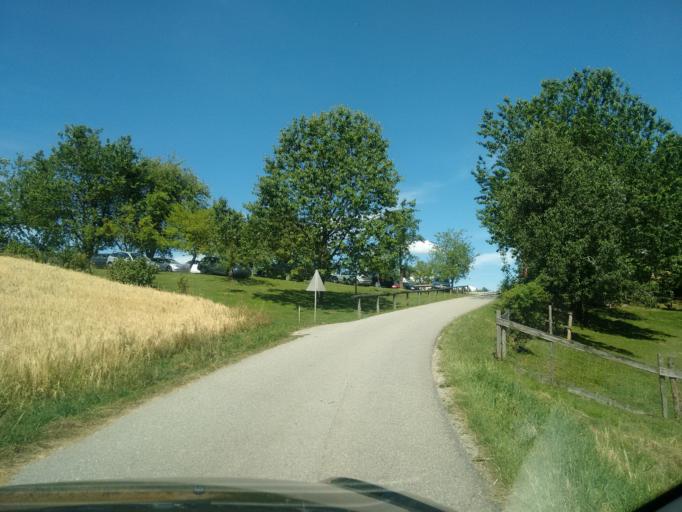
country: AT
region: Upper Austria
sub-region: Politischer Bezirk Ried im Innkreis
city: Ried im Innkreis
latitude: 48.2360
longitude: 13.3905
